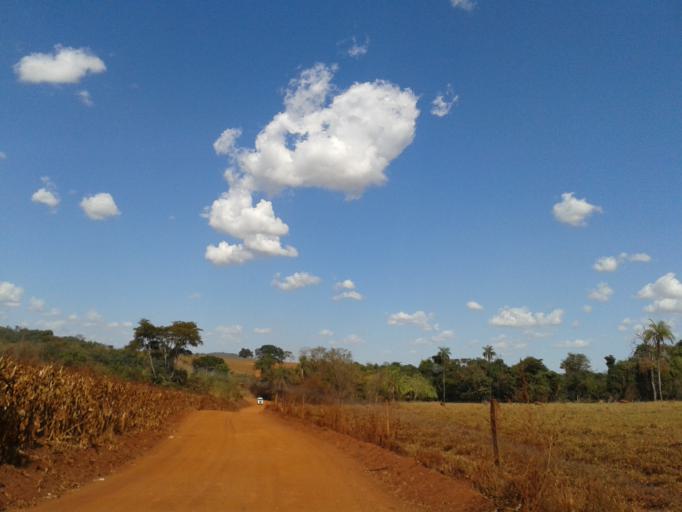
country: BR
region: Minas Gerais
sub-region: Capinopolis
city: Capinopolis
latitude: -18.6085
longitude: -49.4953
